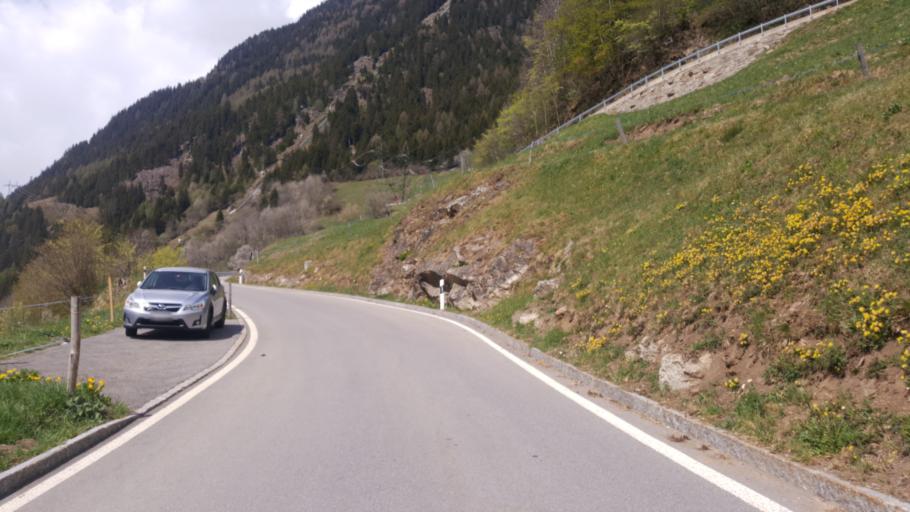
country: CH
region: Ticino
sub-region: Leventina District
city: Airolo
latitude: 46.5202
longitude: 8.6814
